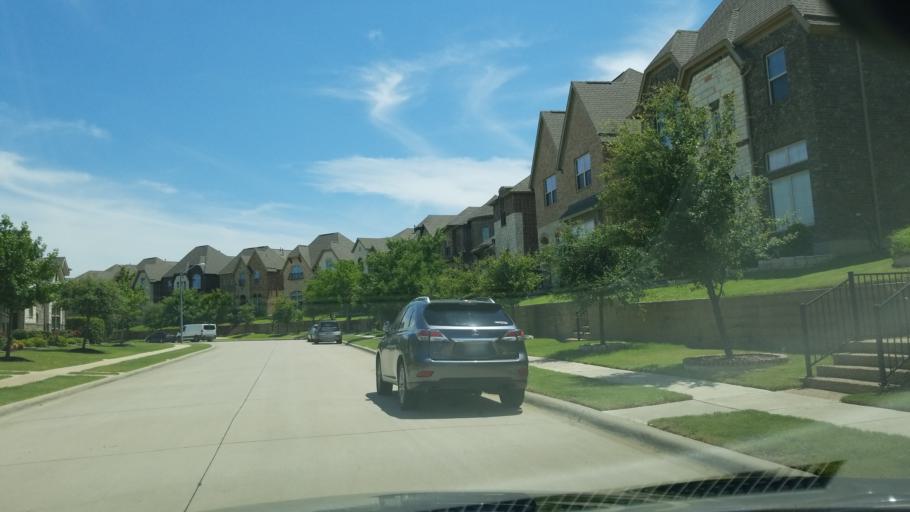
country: US
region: Texas
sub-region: Dallas County
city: Coppell
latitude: 32.8773
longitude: -96.9971
